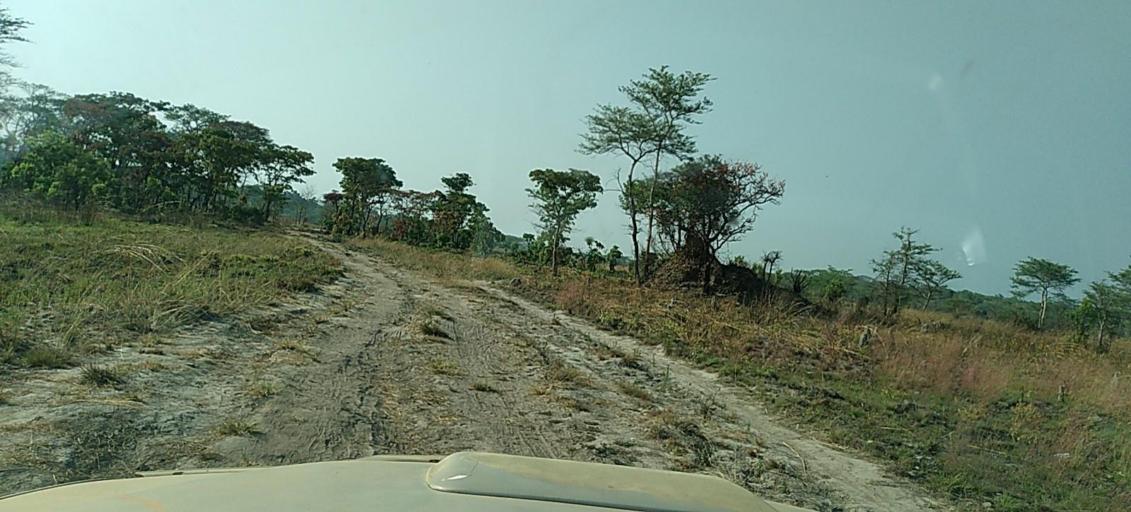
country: ZM
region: North-Western
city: Kasempa
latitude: -13.1885
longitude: 25.9686
